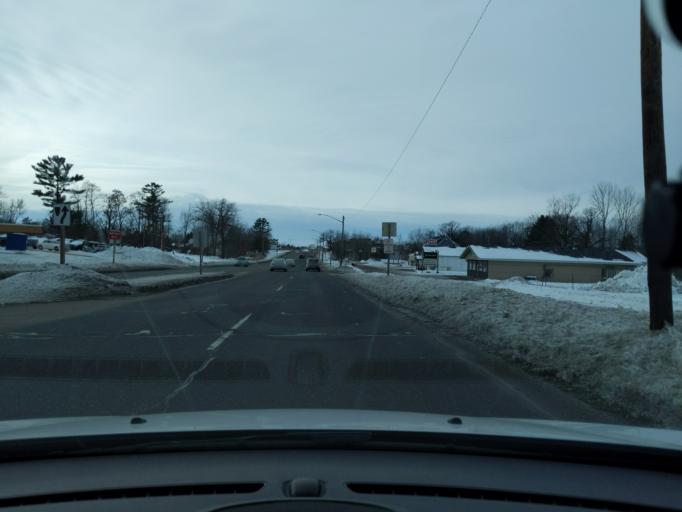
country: US
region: Wisconsin
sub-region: Barron County
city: Turtle Lake
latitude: 45.3991
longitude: -92.1446
